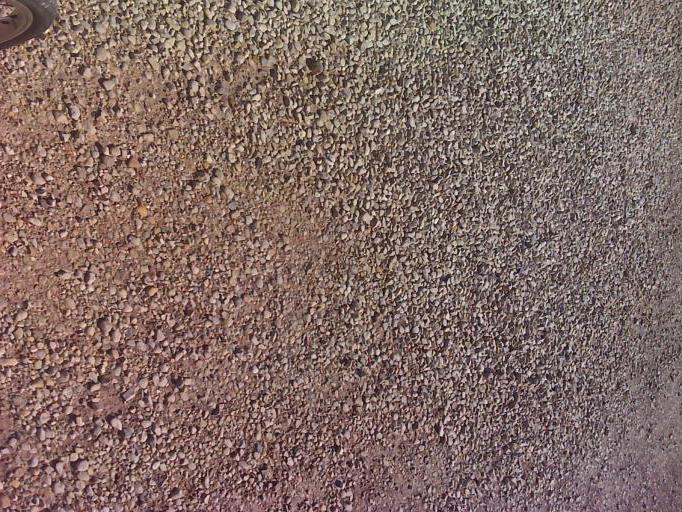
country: FR
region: Nord-Pas-de-Calais
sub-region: Departement du Nord
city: Lambersart
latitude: 50.6478
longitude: 3.0457
